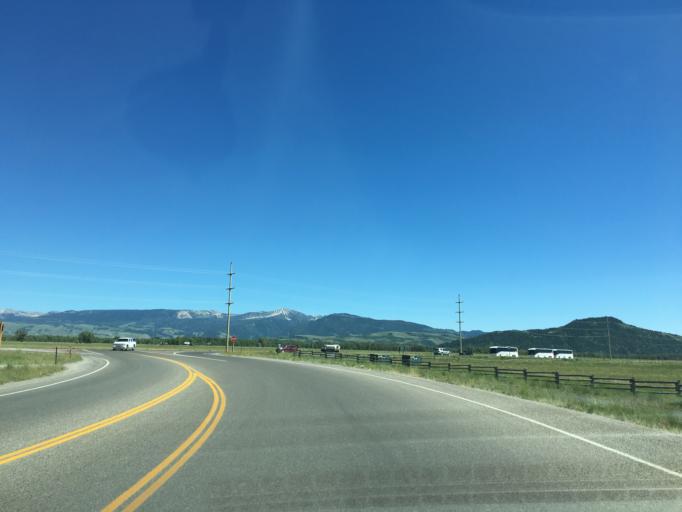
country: US
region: Wyoming
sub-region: Teton County
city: Moose Wilson Road
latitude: 43.5833
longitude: -110.8232
